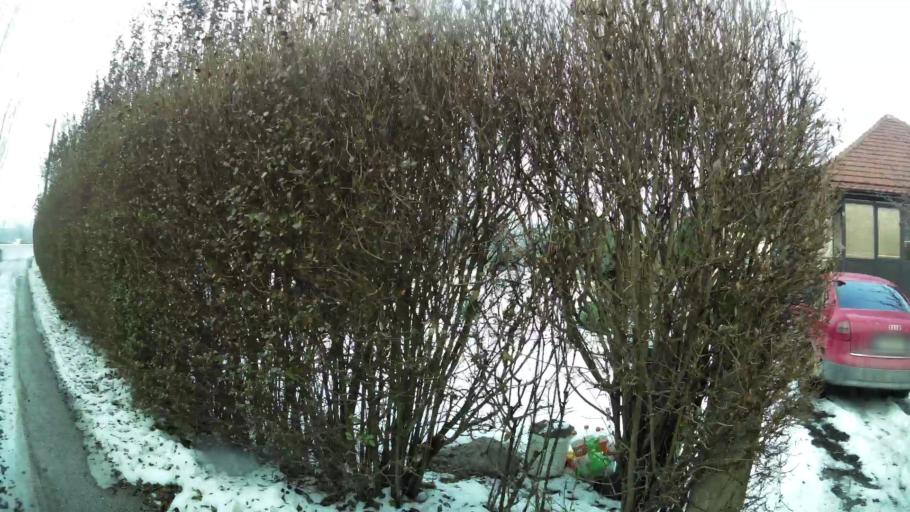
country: MK
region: Ilinden
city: Jurumleri
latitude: 41.9738
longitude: 21.5399
